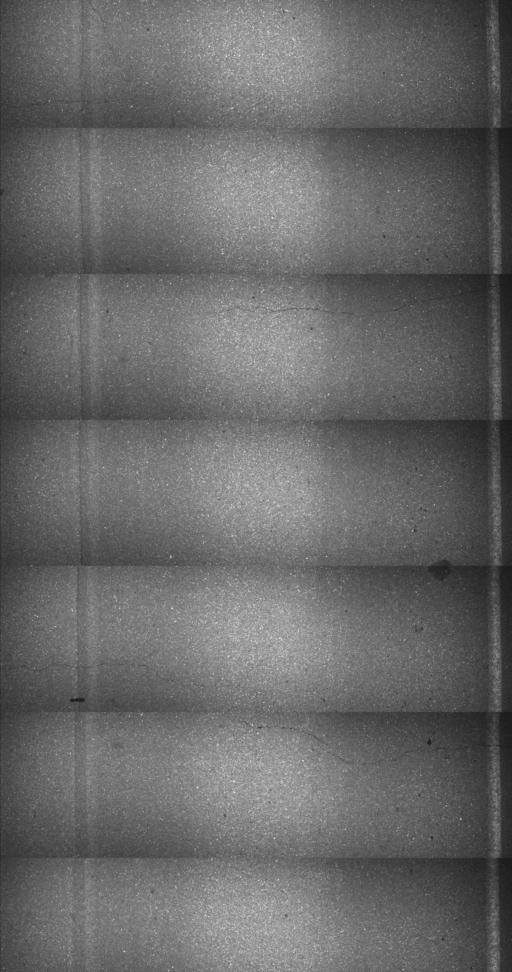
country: US
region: Vermont
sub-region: Caledonia County
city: Lyndonville
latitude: 44.8035
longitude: -71.9179
